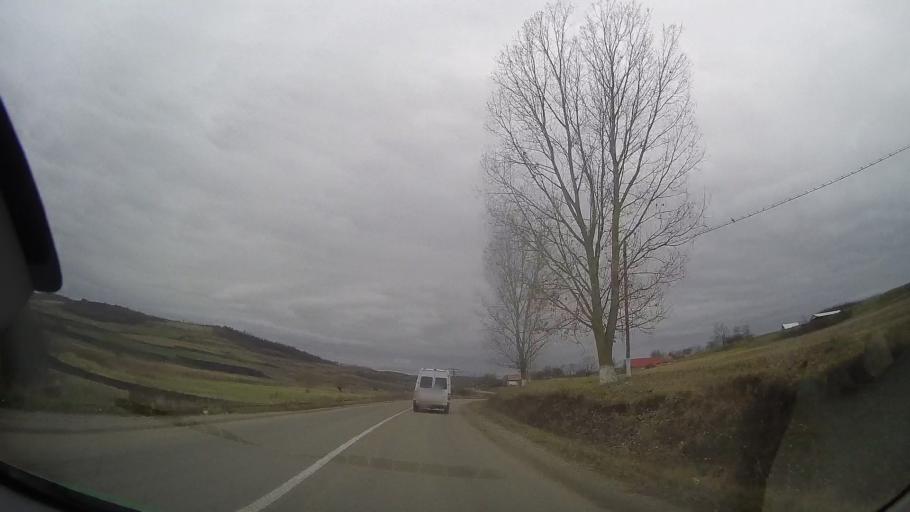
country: RO
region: Cluj
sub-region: Comuna Catina
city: Catina
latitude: 46.7997
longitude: 24.2139
